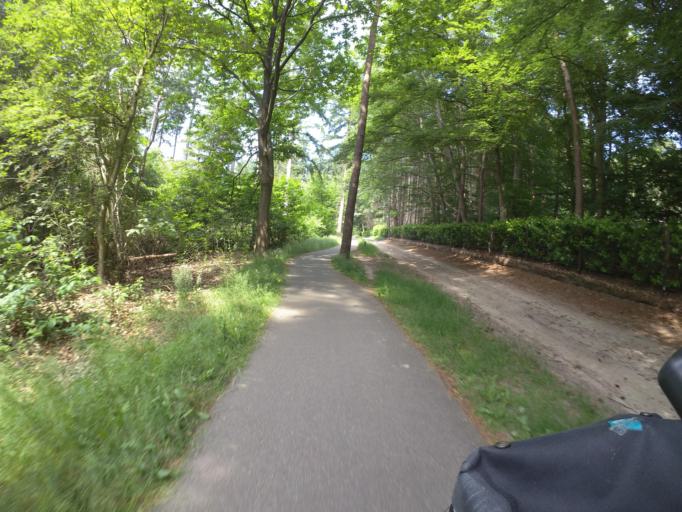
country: NL
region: Overijssel
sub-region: Gemeente Twenterand
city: Den Ham
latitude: 52.3722
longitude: 6.4313
